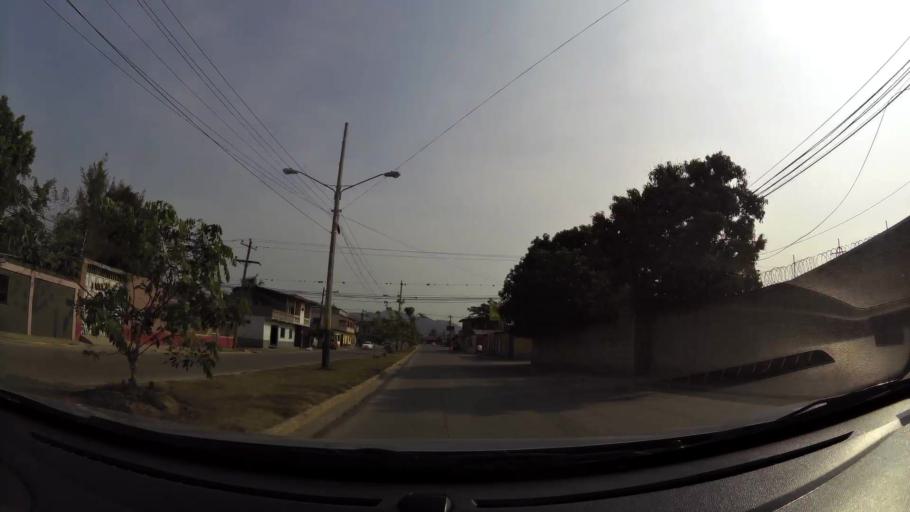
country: HN
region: Comayagua
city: Comayagua
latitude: 14.4525
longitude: -87.6297
